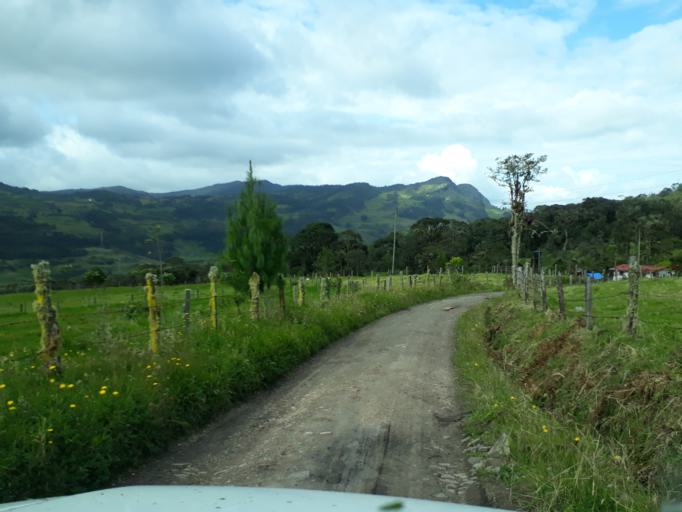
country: CO
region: Cundinamarca
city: Guasca
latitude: 4.8137
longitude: -73.7754
